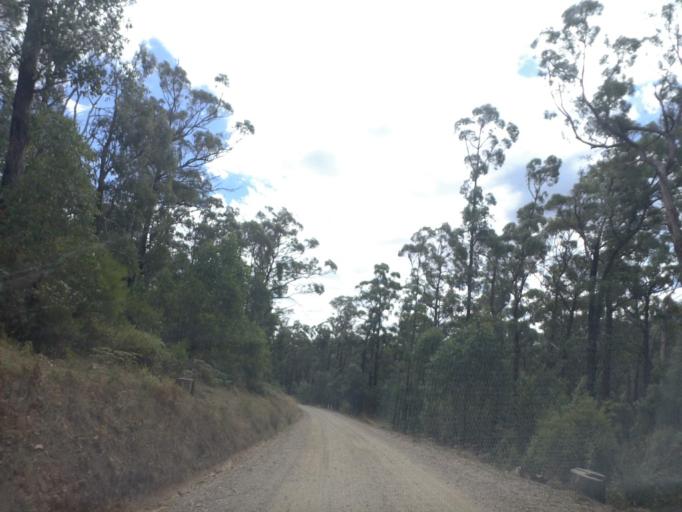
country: AU
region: Victoria
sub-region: Murrindindi
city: Alexandra
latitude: -37.4518
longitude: 145.7585
